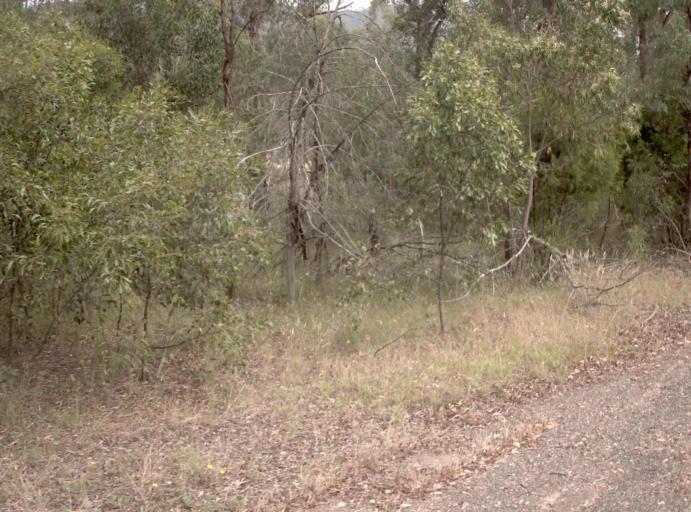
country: AU
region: Victoria
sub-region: Wellington
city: Heyfield
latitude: -37.7510
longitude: 146.6692
